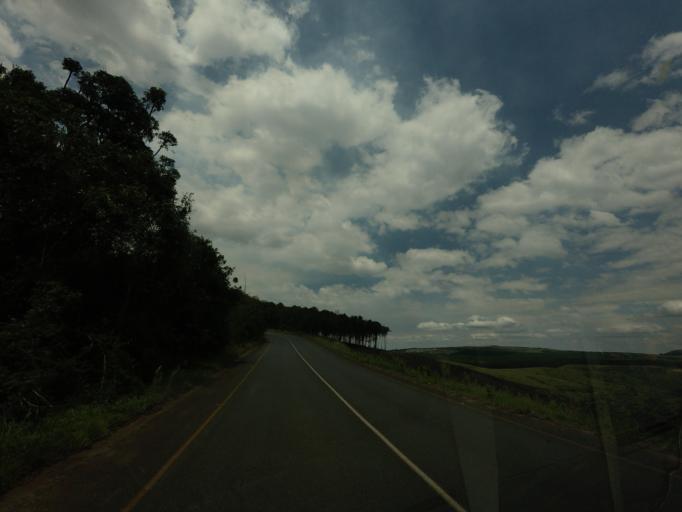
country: ZA
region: Mpumalanga
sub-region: Ehlanzeni District
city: Graksop
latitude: -24.9436
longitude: 30.8109
